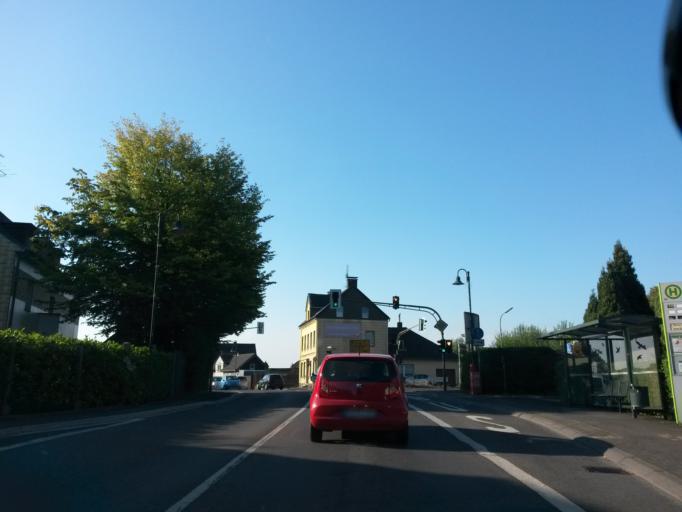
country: DE
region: North Rhine-Westphalia
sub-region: Regierungsbezirk Koln
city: Rosrath
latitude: 50.9310
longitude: 7.1747
